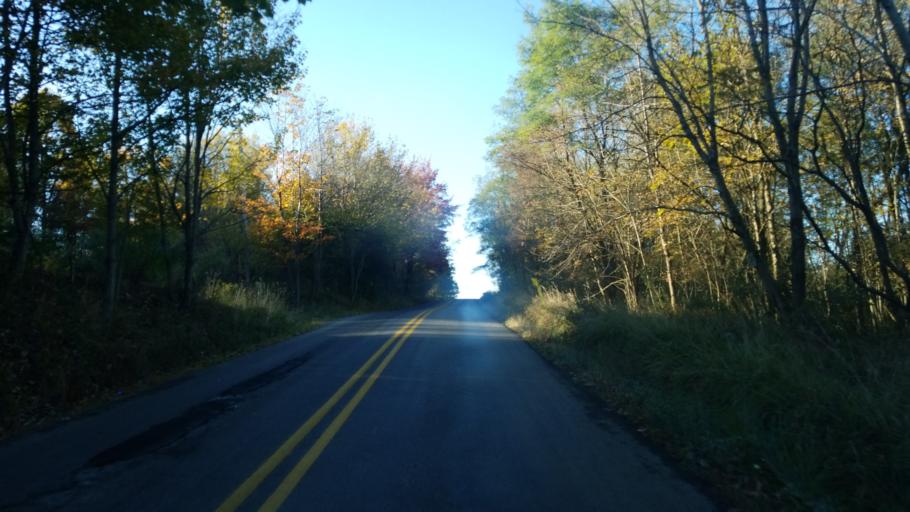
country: US
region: Pennsylvania
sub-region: Indiana County
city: Johnsonburg
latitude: 40.8997
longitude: -78.8962
